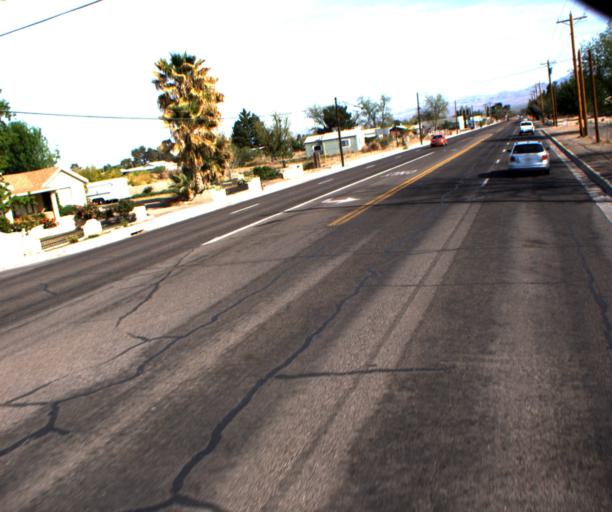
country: US
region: Arizona
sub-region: Graham County
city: Safford
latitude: 32.8168
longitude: -109.7076
